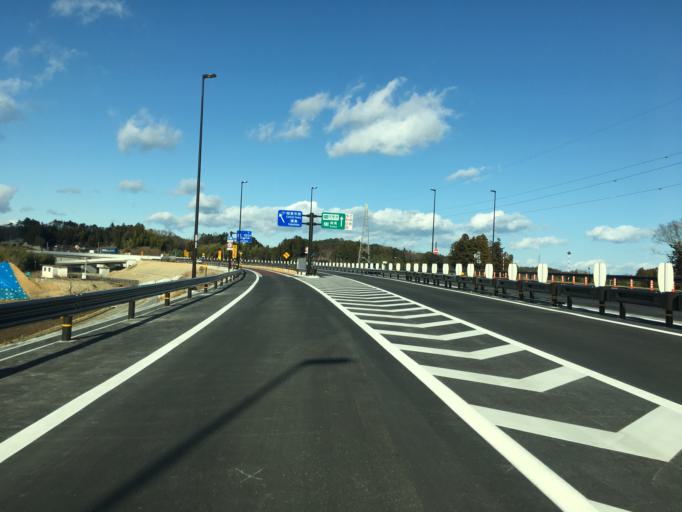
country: JP
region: Miyagi
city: Marumori
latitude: 37.7802
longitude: 140.9019
